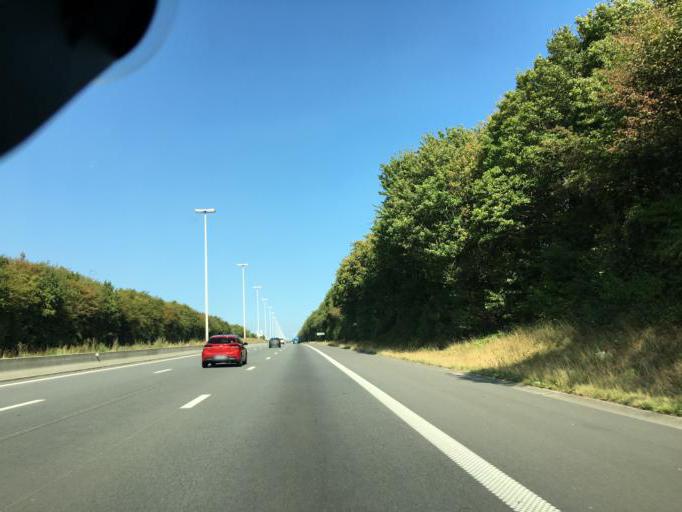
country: BE
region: Wallonia
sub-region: Province de Liege
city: Wanze
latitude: 50.5738
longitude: 5.1960
